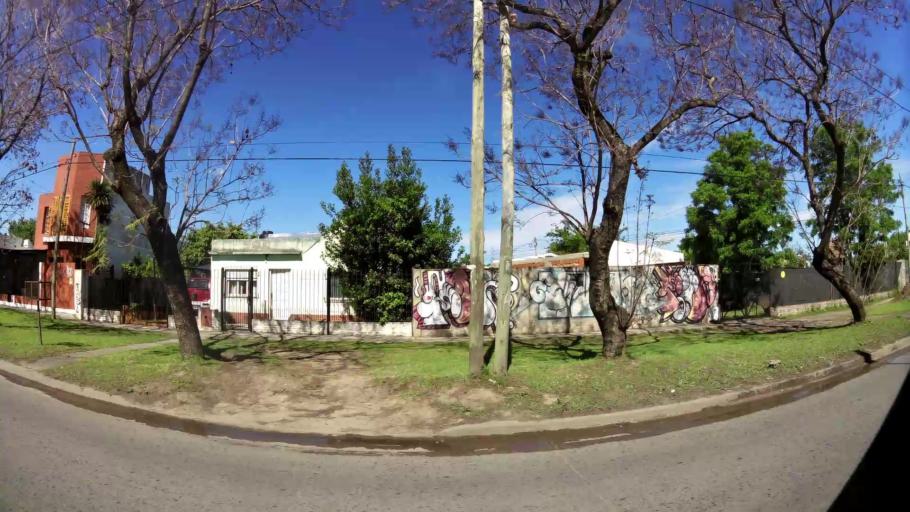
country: AR
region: Buenos Aires
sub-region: Partido de Almirante Brown
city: Adrogue
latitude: -34.7984
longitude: -58.3644
